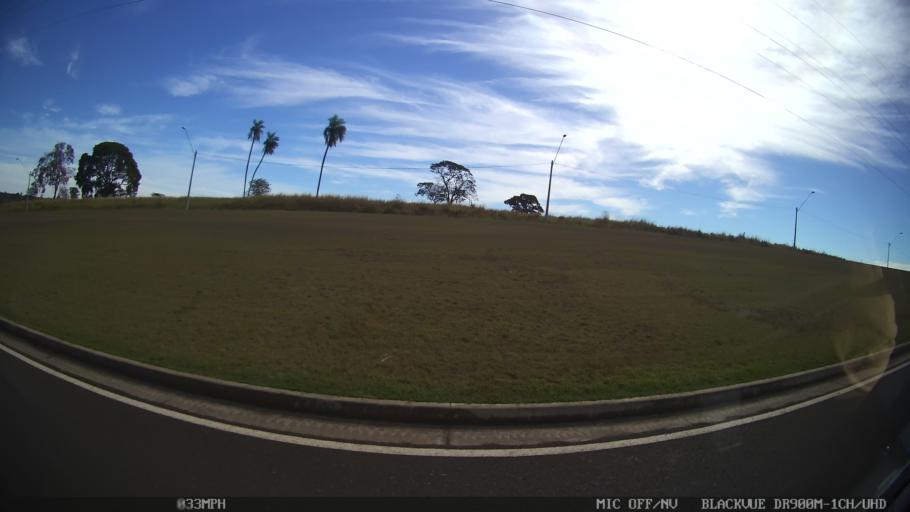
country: BR
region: Sao Paulo
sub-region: Sao Jose Do Rio Preto
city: Sao Jose do Rio Preto
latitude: -20.8570
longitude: -49.3790
